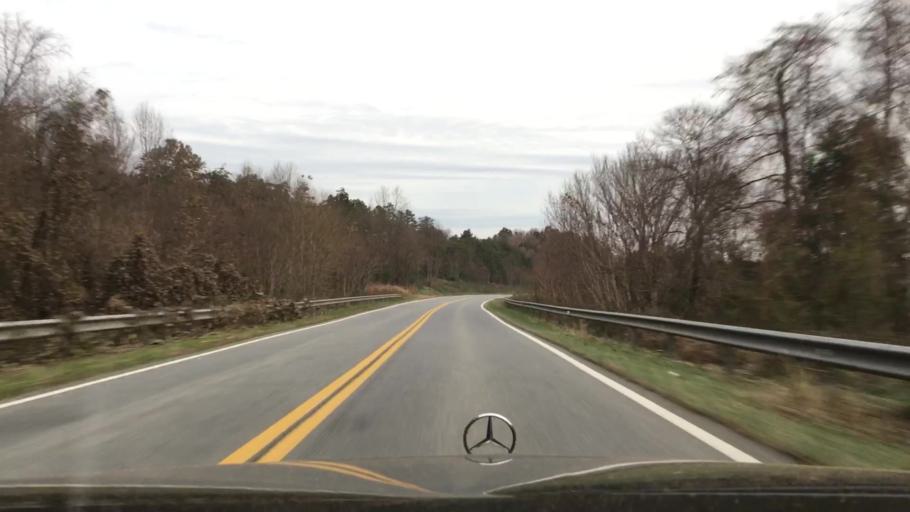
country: US
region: Virginia
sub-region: Campbell County
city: Altavista
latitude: 37.1691
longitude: -79.2957
